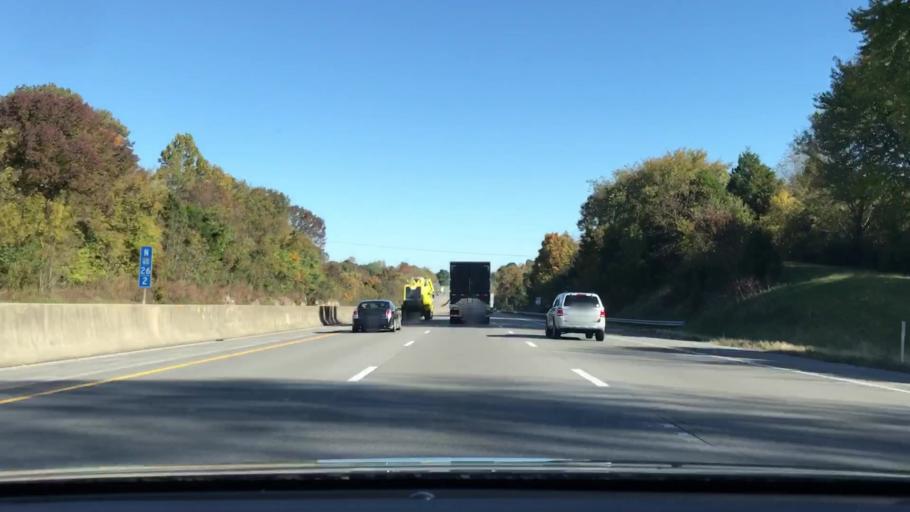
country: US
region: Kentucky
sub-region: Warren County
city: Bowling Green
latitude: 36.9837
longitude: -86.3876
